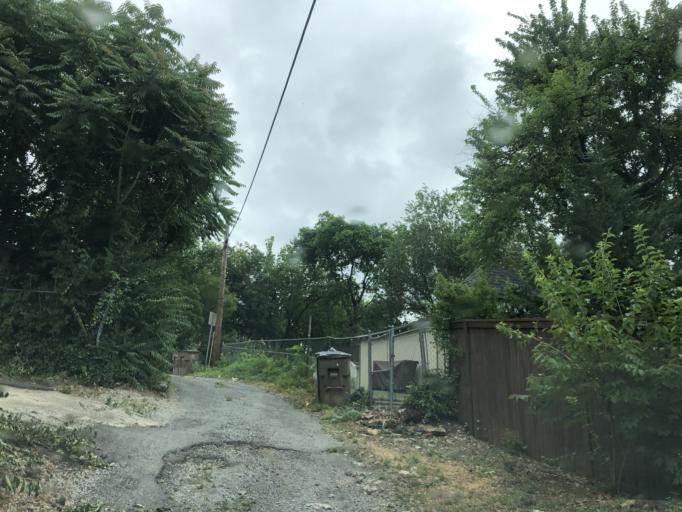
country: US
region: Tennessee
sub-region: Davidson County
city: Nashville
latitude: 36.1312
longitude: -86.8135
